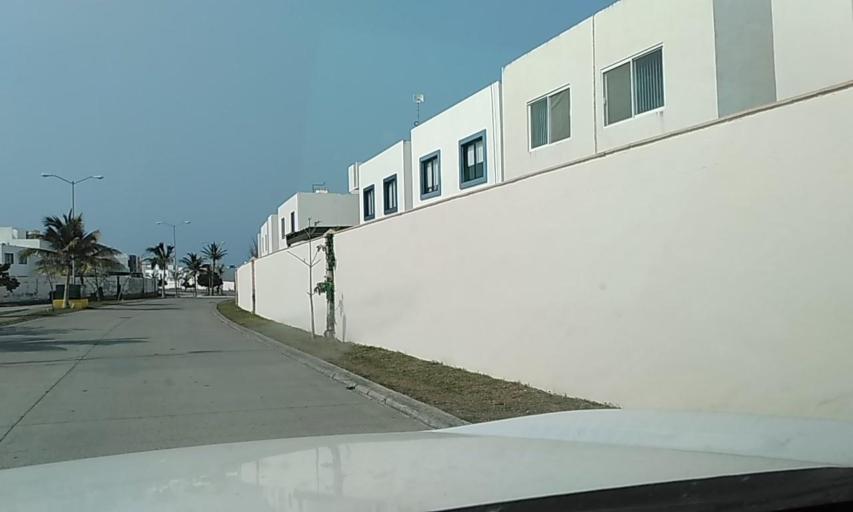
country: MX
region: Veracruz
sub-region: Alvarado
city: Playa de la Libertad
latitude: 19.0504
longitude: -96.0614
